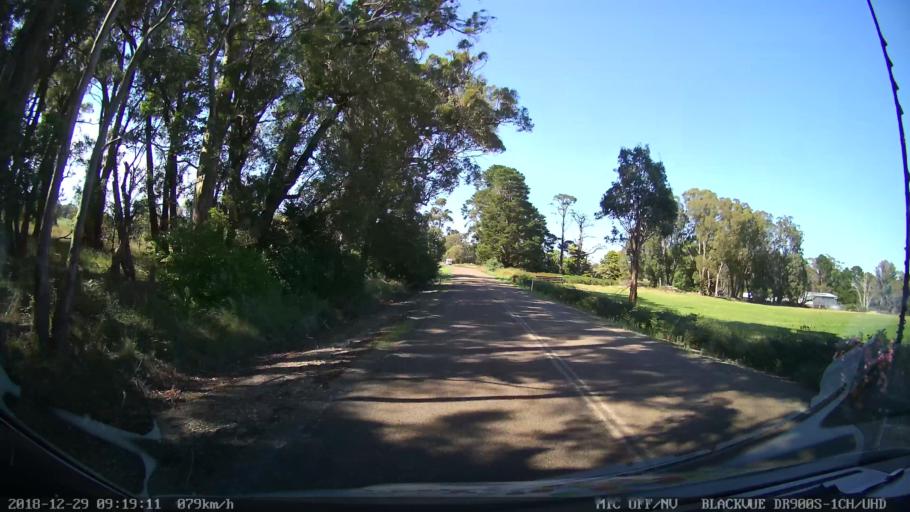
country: AU
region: New South Wales
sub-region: Upper Lachlan Shire
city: Crookwell
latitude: -34.4787
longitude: 149.4301
